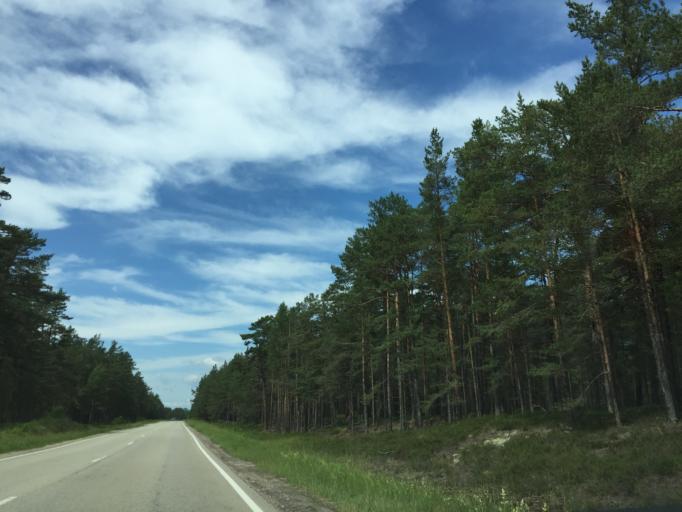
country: LV
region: Engure
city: Smarde
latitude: 57.0519
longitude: 23.3275
